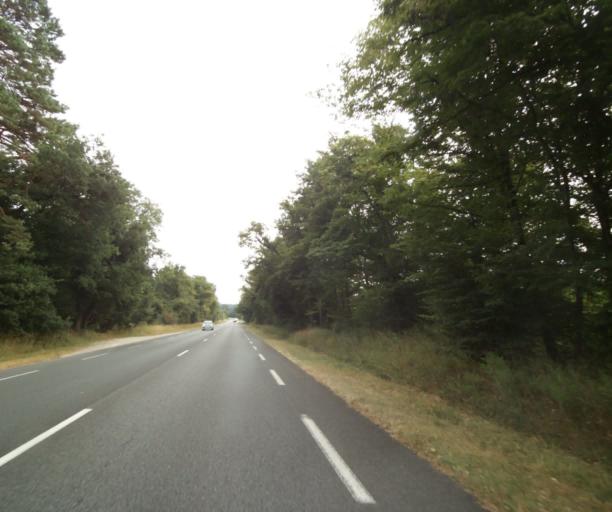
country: FR
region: Ile-de-France
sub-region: Departement de Seine-et-Marne
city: Bois-le-Roi
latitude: 48.4445
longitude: 2.6890
